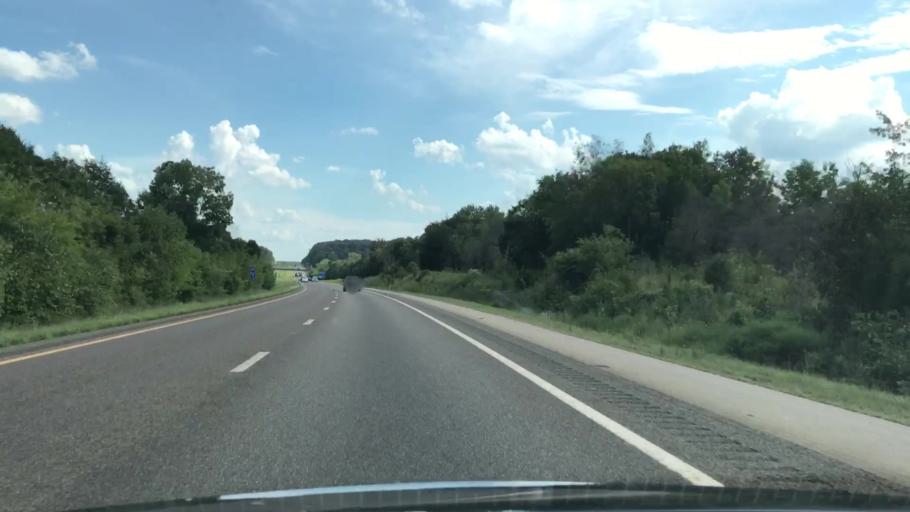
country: US
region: Tennessee
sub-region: Maury County
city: Columbia
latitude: 35.5499
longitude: -86.9082
